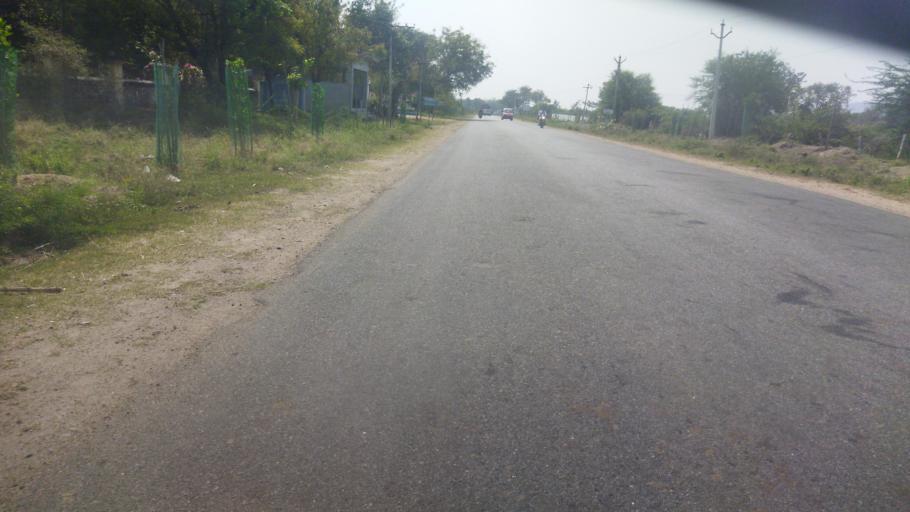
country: IN
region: Telangana
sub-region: Nalgonda
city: Nalgonda
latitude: 17.0954
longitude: 79.2857
